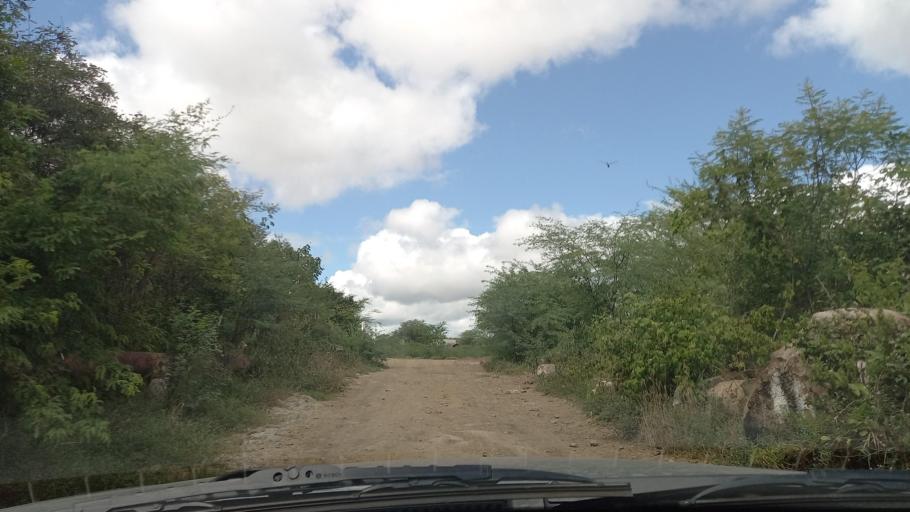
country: BR
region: Pernambuco
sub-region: Caruaru
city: Caruaru
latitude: -8.2511
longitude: -35.9816
